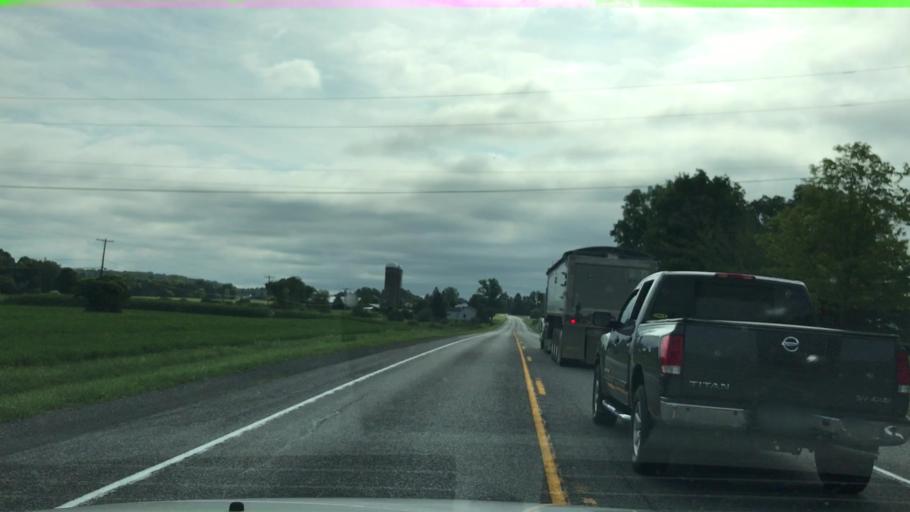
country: US
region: New York
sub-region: Erie County
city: Alden
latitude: 42.8354
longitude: -78.4143
